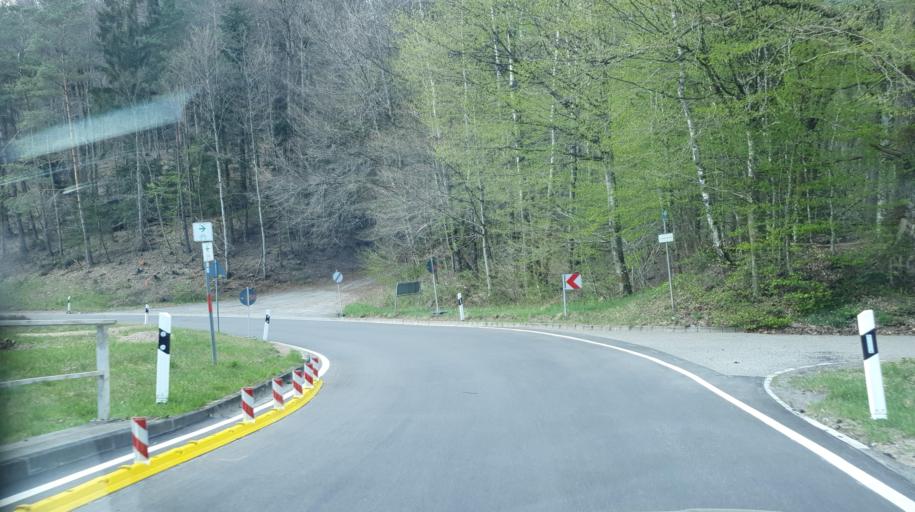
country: DE
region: Rheinland-Pfalz
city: Leimen
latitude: 49.2830
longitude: 7.7399
